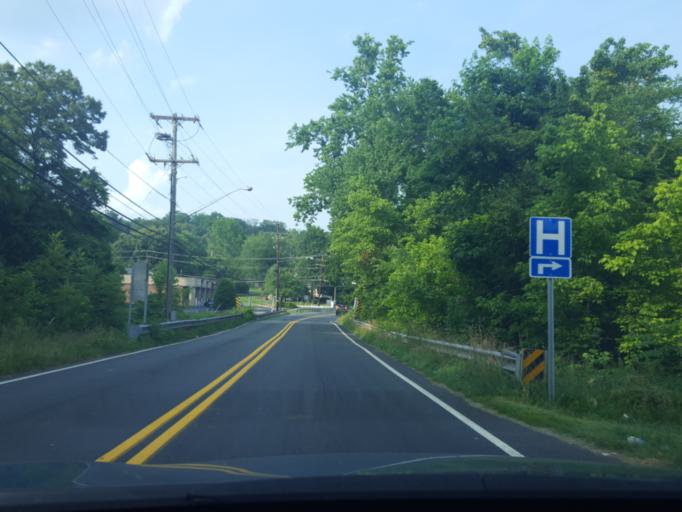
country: US
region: Maryland
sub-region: Prince George's County
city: Friendly
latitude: 38.7411
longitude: -77.0001
